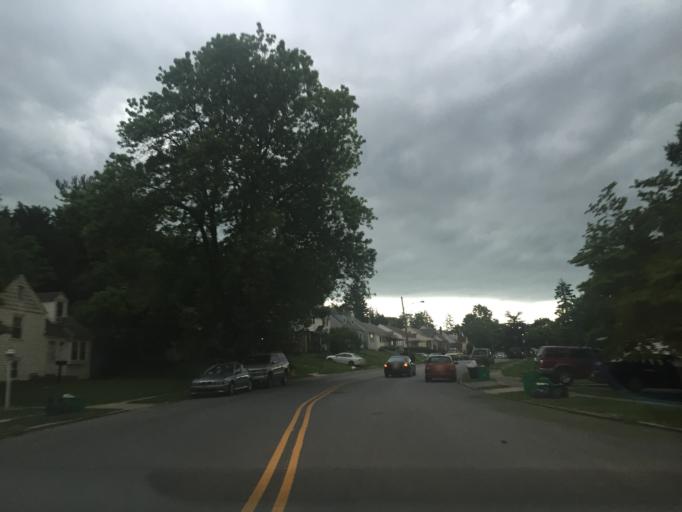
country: US
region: Pennsylvania
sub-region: York County
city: North York
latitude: 39.9682
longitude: -76.7438
